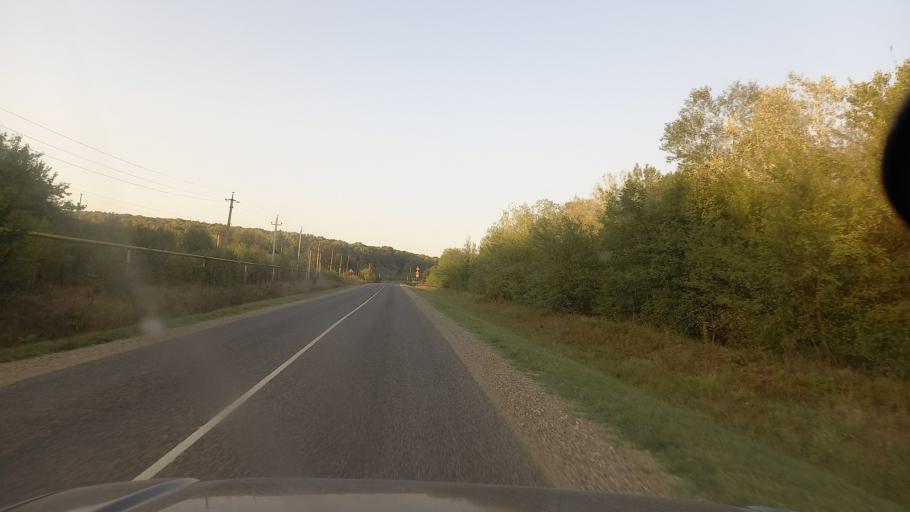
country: RU
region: Krasnodarskiy
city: Smolenskaya
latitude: 44.7584
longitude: 38.7679
